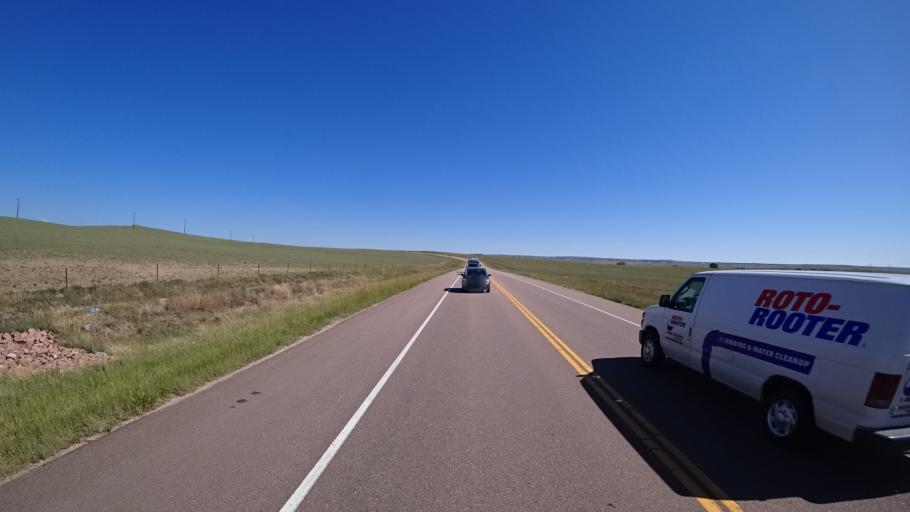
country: US
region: Colorado
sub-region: El Paso County
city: Security-Widefield
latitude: 38.7877
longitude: -104.6585
